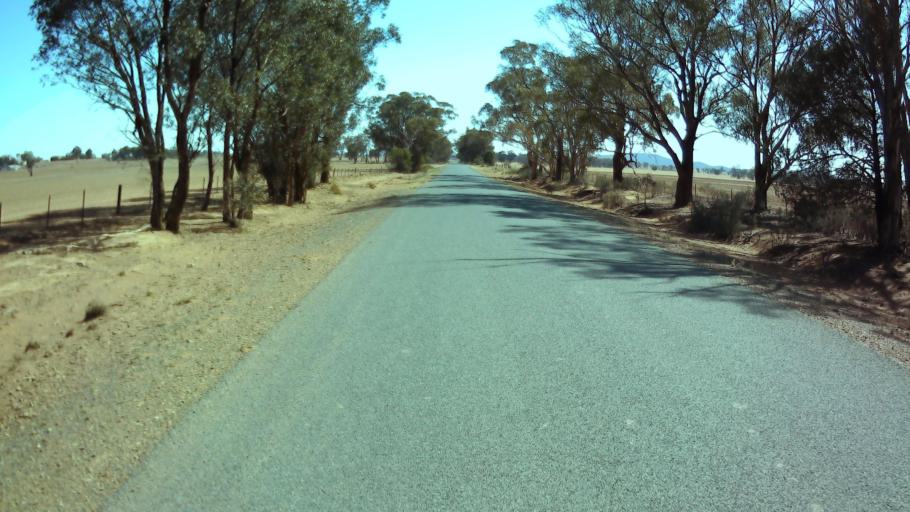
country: AU
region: New South Wales
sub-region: Weddin
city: Grenfell
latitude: -33.7455
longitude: 147.8781
